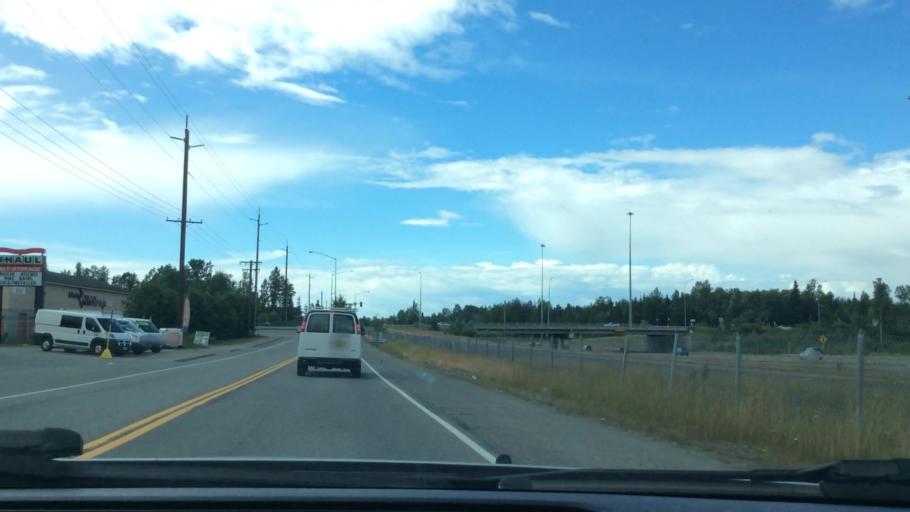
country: US
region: Alaska
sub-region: Anchorage Municipality
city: Anchorage
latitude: 61.2242
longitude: -149.7736
